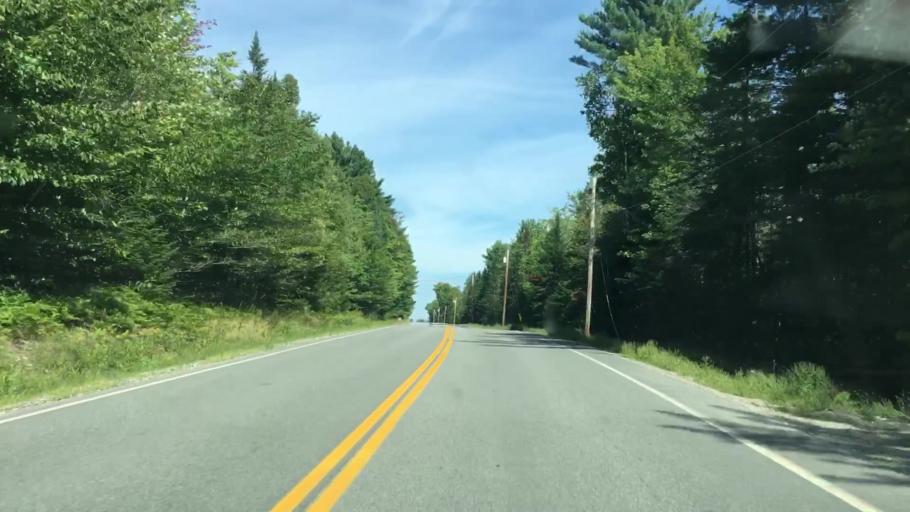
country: US
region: Maine
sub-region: Penobscot County
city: Howland
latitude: 45.2055
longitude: -68.8079
